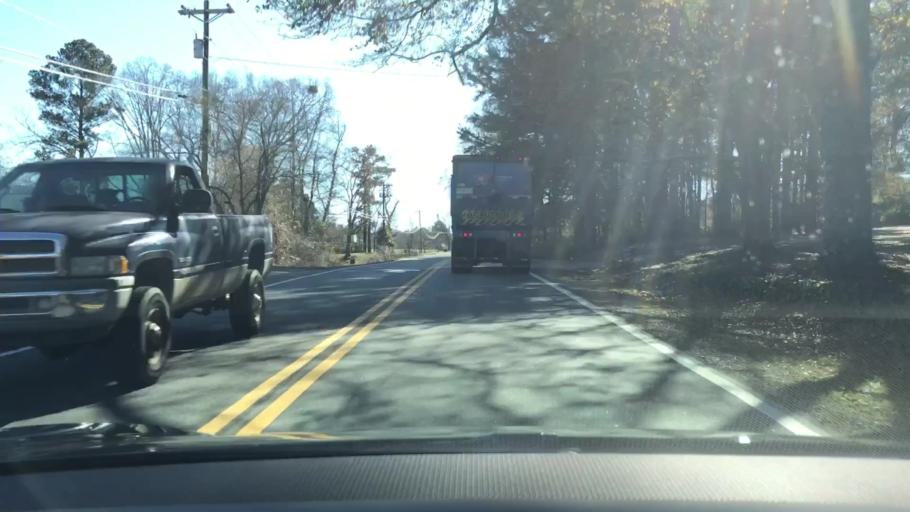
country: US
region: Georgia
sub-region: Barrow County
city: Auburn
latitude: 33.9332
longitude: -83.8320
